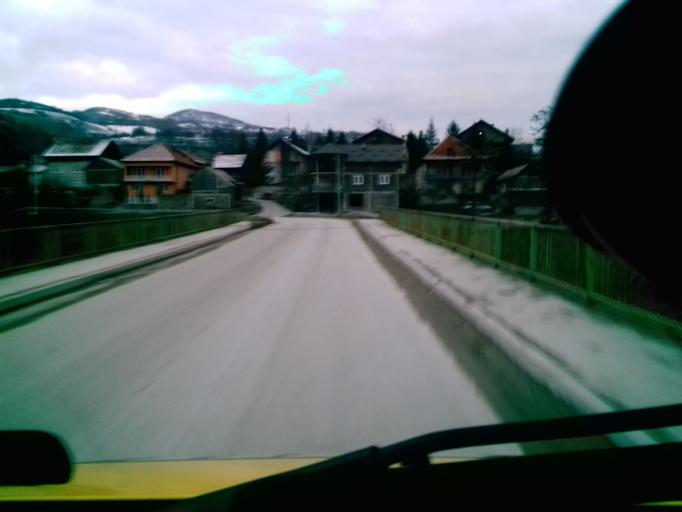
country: BA
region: Federation of Bosnia and Herzegovina
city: Zenica
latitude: 44.1702
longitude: 17.9728
